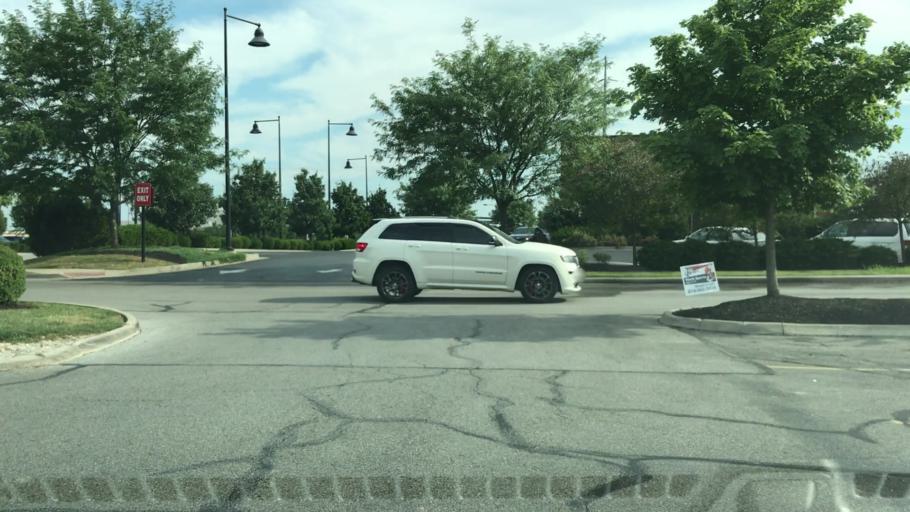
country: US
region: Ohio
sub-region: Franklin County
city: Grove City
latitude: 39.8796
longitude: -83.0393
